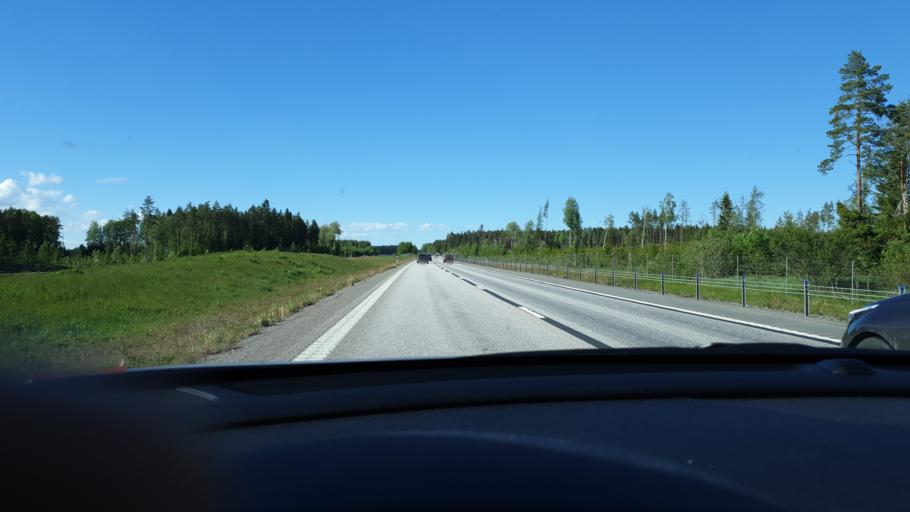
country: SE
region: Uppsala
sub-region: Tierps Kommun
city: Tierp
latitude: 60.2638
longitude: 17.5006
